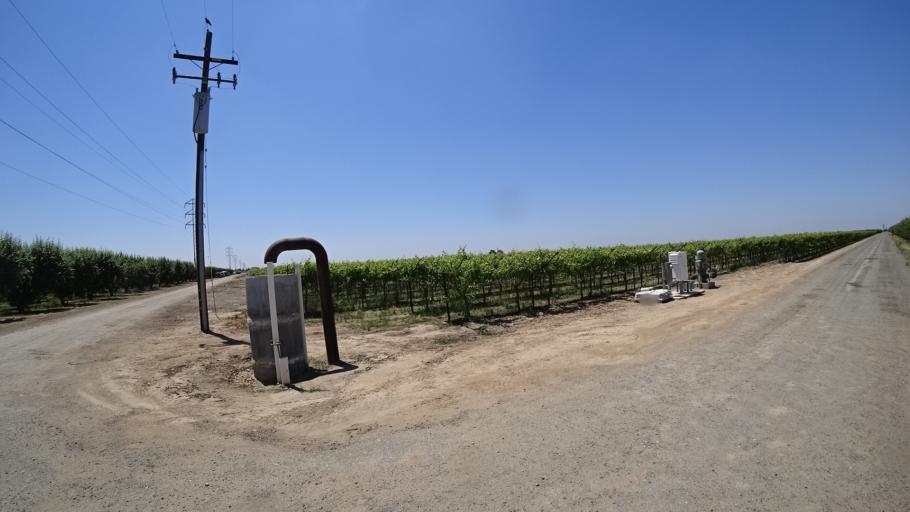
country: US
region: California
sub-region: Fresno County
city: Kingsburg
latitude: 36.4706
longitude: -119.5913
